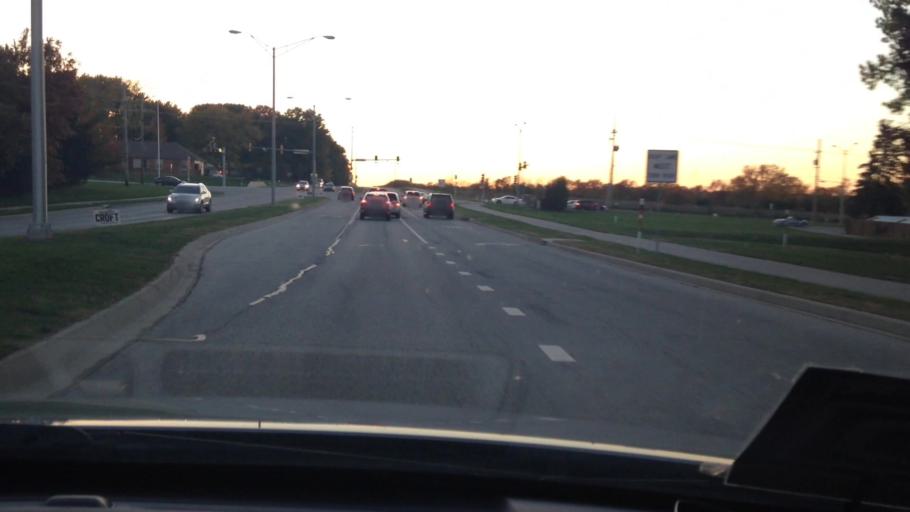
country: US
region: Kansas
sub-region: Johnson County
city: Lenexa
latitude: 38.8692
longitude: -94.7220
